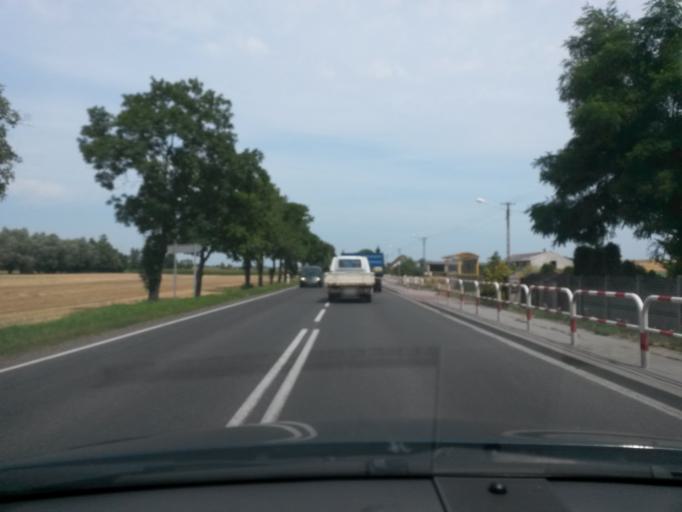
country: PL
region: Greater Poland Voivodeship
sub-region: Powiat gostynski
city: Krobia
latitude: 51.8180
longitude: 17.0015
